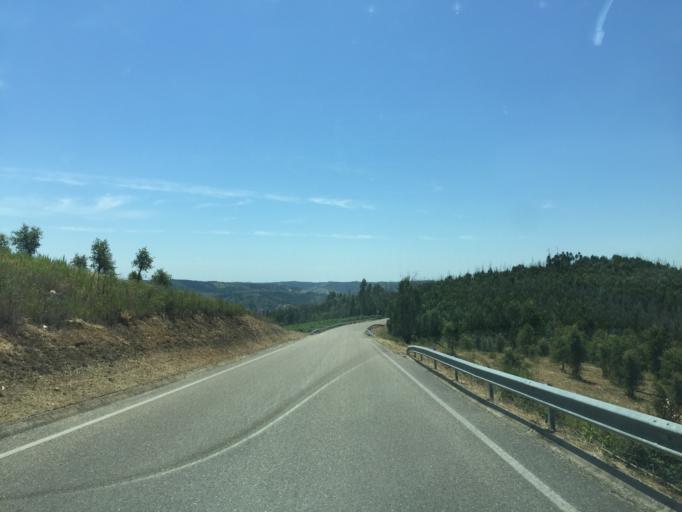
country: PT
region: Santarem
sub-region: Ferreira do Zezere
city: Ferreira do Zezere
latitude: 39.5855
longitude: -8.2971
